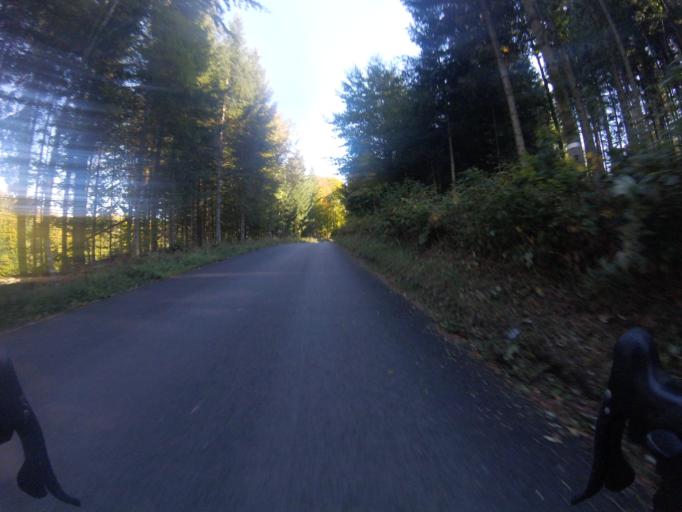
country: CH
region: Bern
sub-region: Bern-Mittelland District
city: Kirchlindach
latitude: 47.0137
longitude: 7.4016
